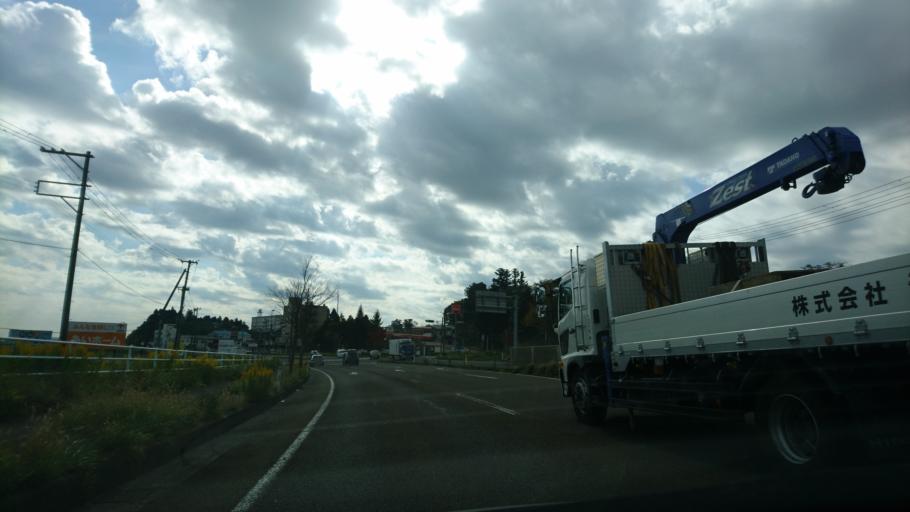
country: JP
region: Miyagi
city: Tomiya
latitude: 38.4542
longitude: 140.8797
